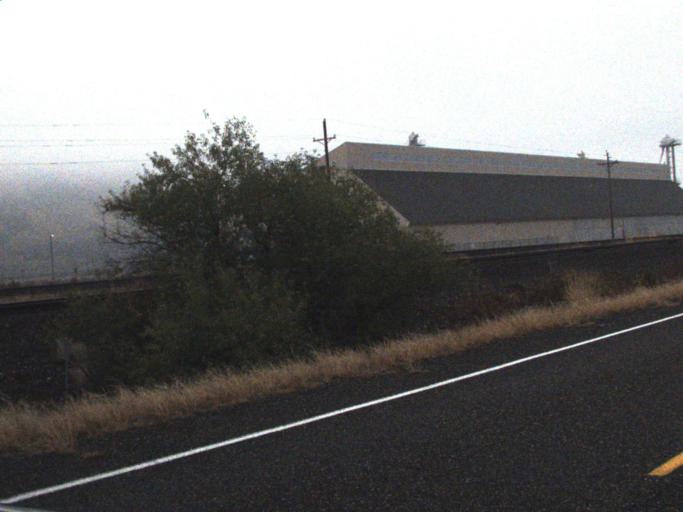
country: US
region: Washington
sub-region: Asotin County
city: Clarkston Heights-Vineland
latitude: 46.4282
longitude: -117.1160
